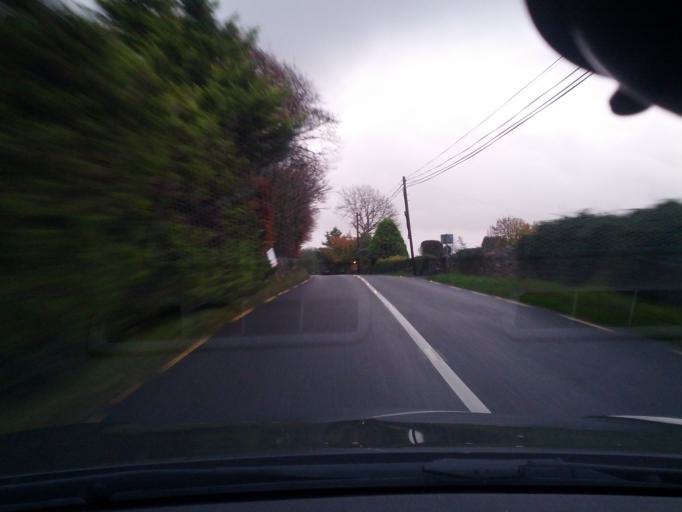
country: IE
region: Connaught
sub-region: County Galway
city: Athenry
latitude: 53.3084
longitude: -8.7905
